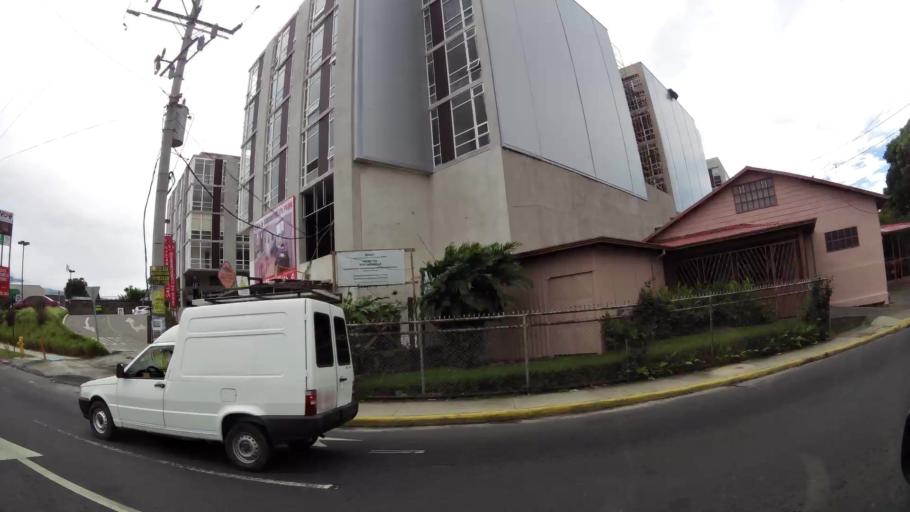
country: CR
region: San Jose
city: Sabanilla
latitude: 9.9428
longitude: -84.0424
